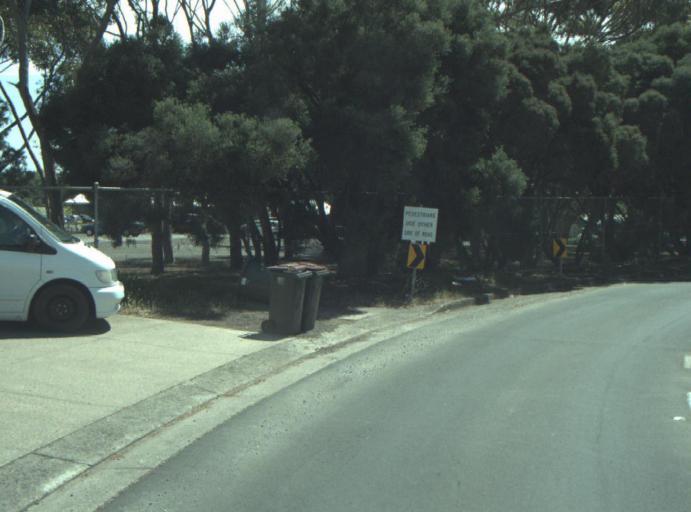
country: AU
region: Victoria
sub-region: Greater Geelong
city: Geelong West
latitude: -38.1479
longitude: 144.3271
